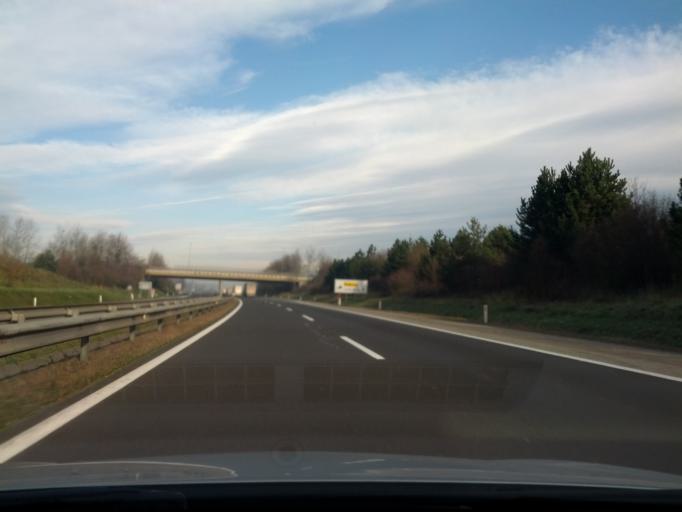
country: SI
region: Hoce-Slivnica
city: Rogoza
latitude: 46.4980
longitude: 15.6704
